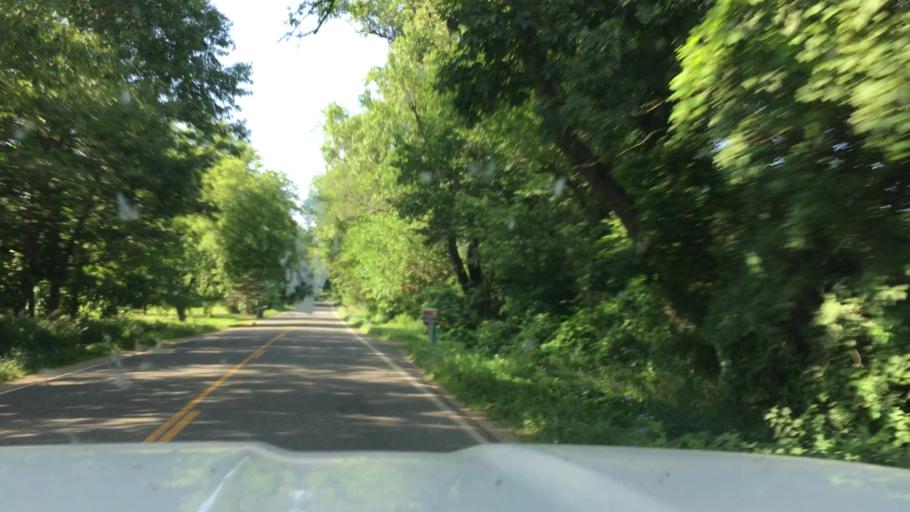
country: US
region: Michigan
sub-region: Barry County
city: Stony Point
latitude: 42.4377
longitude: -85.4544
